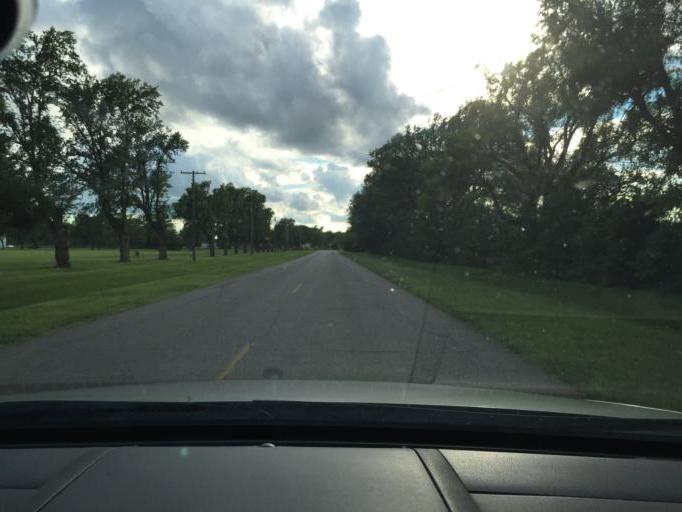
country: US
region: Kansas
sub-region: Reno County
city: Haven
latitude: 37.9264
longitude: -97.8900
